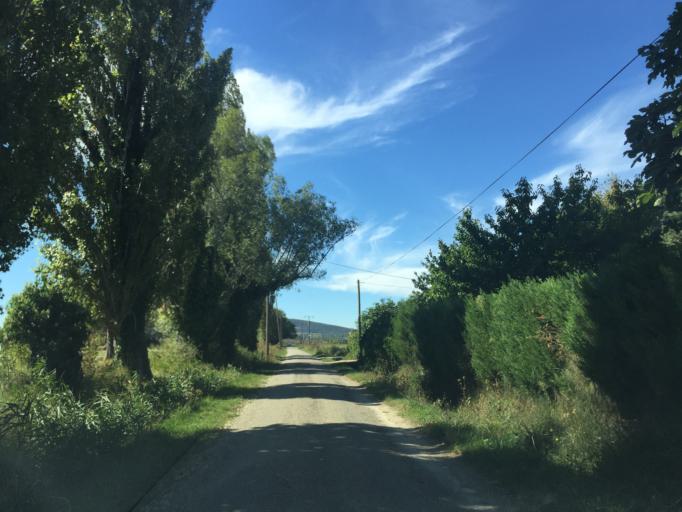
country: FR
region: Provence-Alpes-Cote d'Azur
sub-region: Departement du Vaucluse
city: Piolenc
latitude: 44.1546
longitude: 4.7553
